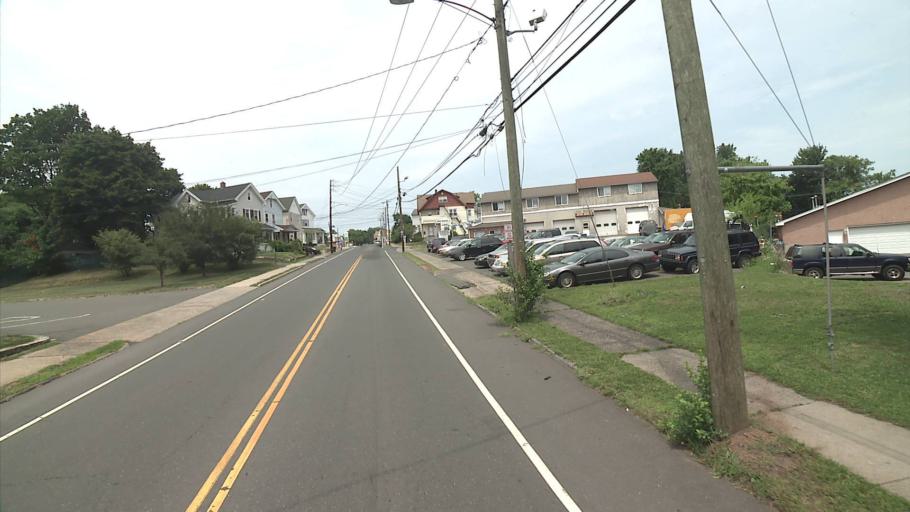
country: US
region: Connecticut
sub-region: Hartford County
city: New Britain
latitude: 41.6512
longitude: -72.7732
